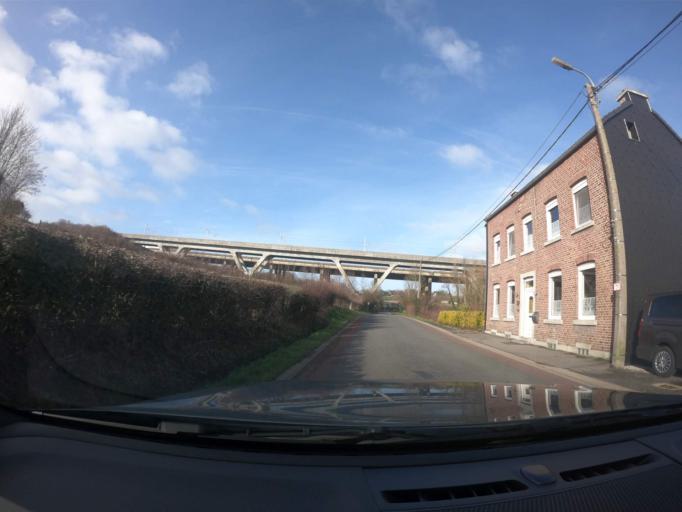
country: BE
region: Wallonia
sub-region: Province de Liege
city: Herve
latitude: 50.6326
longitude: 5.8021
